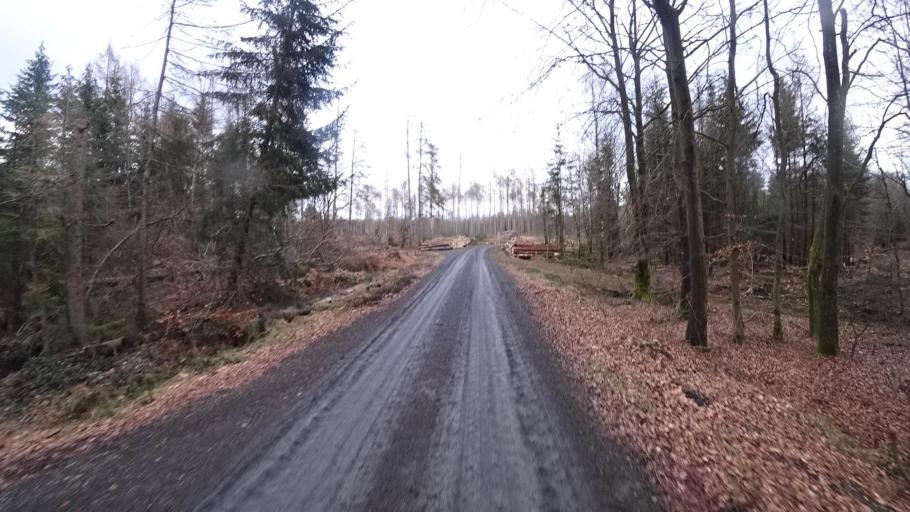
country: DE
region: Rheinland-Pfalz
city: Kadenbach
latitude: 50.4097
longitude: 7.7479
